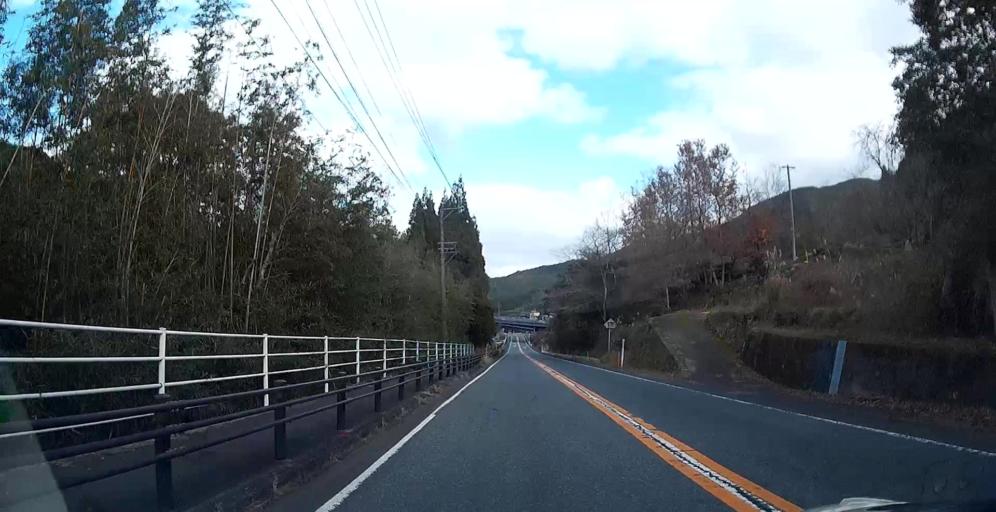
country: JP
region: Kumamoto
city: Yatsushiro
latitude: 32.3813
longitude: 130.5385
